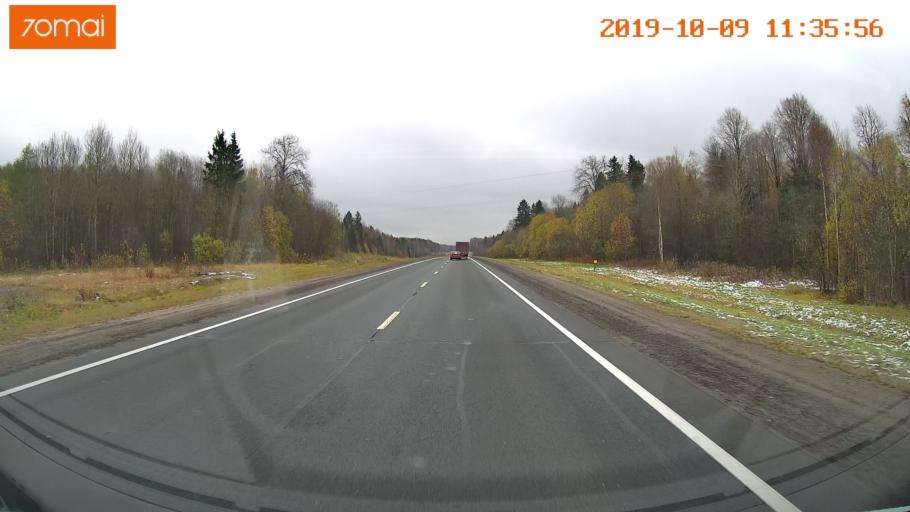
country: RU
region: Vologda
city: Gryazovets
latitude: 58.9971
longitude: 40.1313
